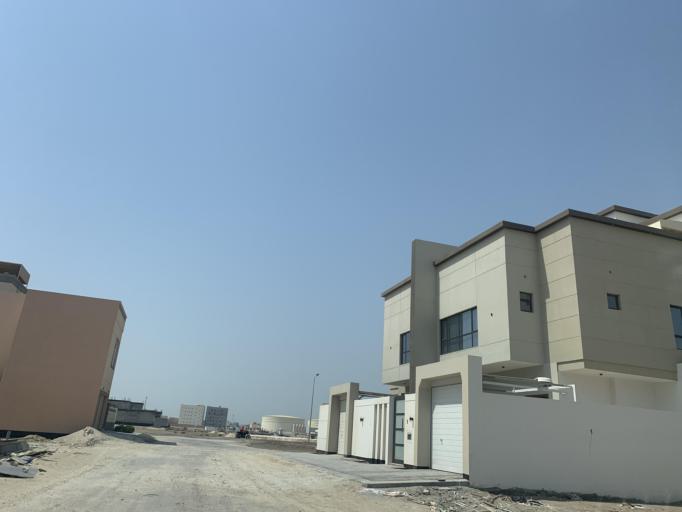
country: BH
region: Manama
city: Jidd Hafs
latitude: 26.2016
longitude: 50.5257
